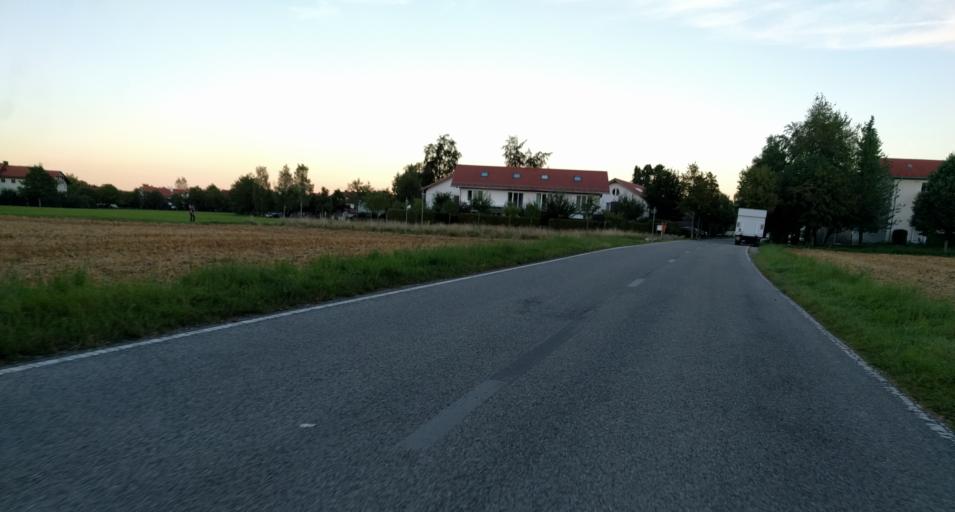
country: DE
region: Bavaria
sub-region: Upper Bavaria
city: Oberhaching
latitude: 48.0249
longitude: 11.5705
